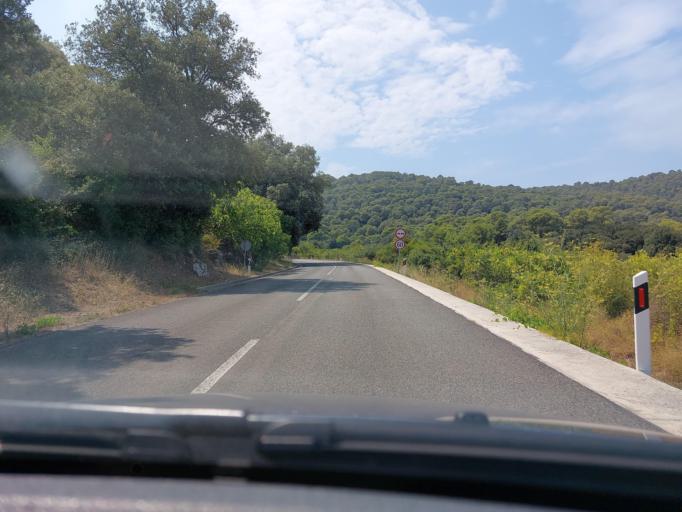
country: HR
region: Dubrovacko-Neretvanska
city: Smokvica
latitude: 42.7539
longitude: 16.8399
